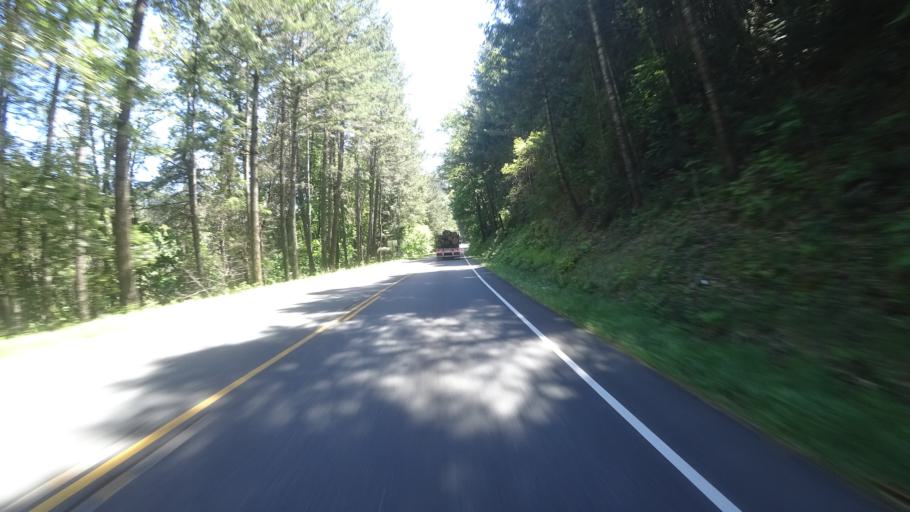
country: US
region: California
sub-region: Humboldt County
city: Willow Creek
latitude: 40.8927
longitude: -123.5775
